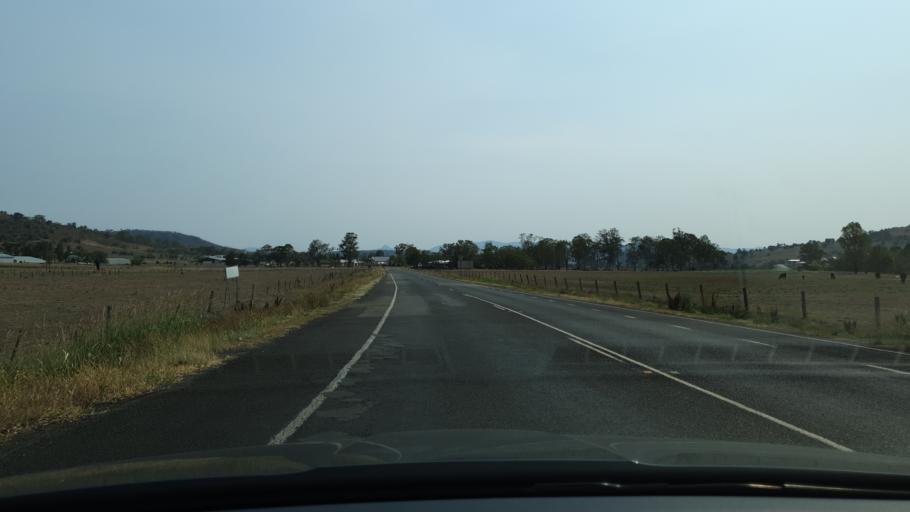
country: AU
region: Queensland
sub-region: Ipswich
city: Deebing Heights
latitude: -28.0087
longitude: 152.6794
